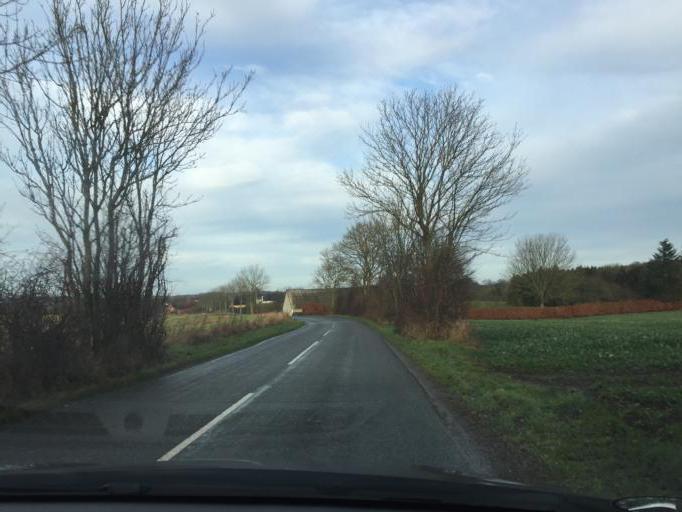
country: DK
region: South Denmark
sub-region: Faaborg-Midtfyn Kommune
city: Ringe
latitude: 55.1775
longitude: 10.4059
